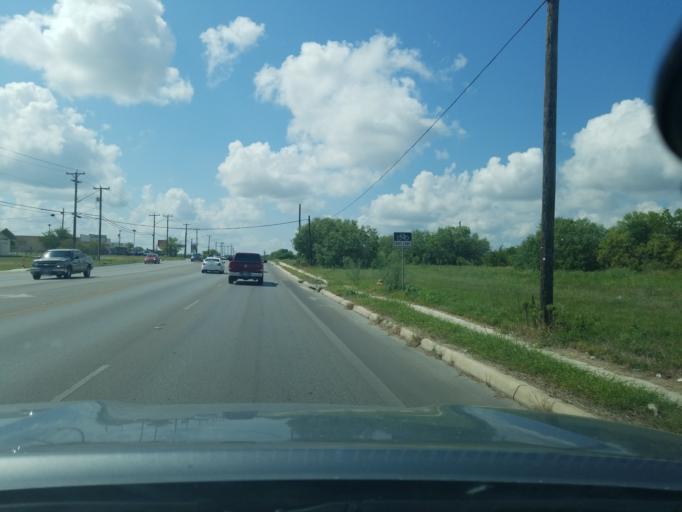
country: US
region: Texas
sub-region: Bexar County
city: San Antonio
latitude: 29.3403
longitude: -98.5342
